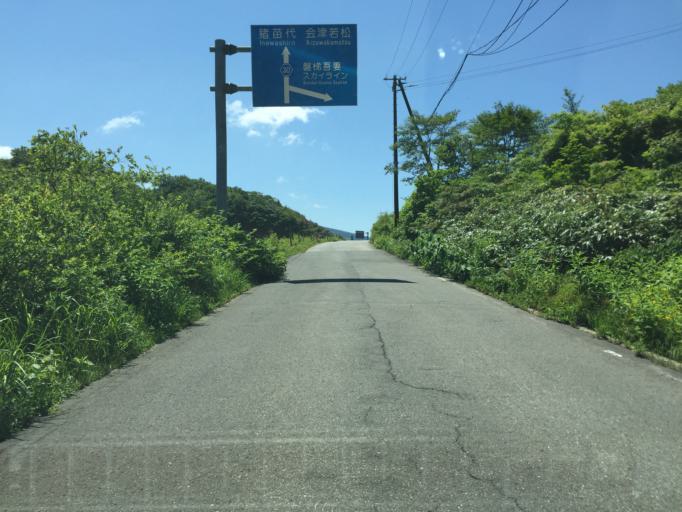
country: JP
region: Fukushima
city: Inawashiro
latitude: 37.6693
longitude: 140.2557
